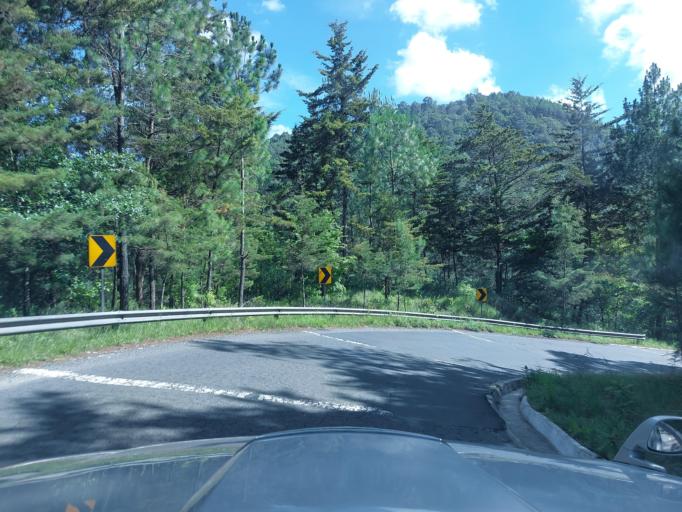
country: GT
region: Chimaltenango
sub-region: Municipio de Santa Cruz Balanya
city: Santa Cruz Balanya
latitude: 14.6934
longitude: -90.8984
